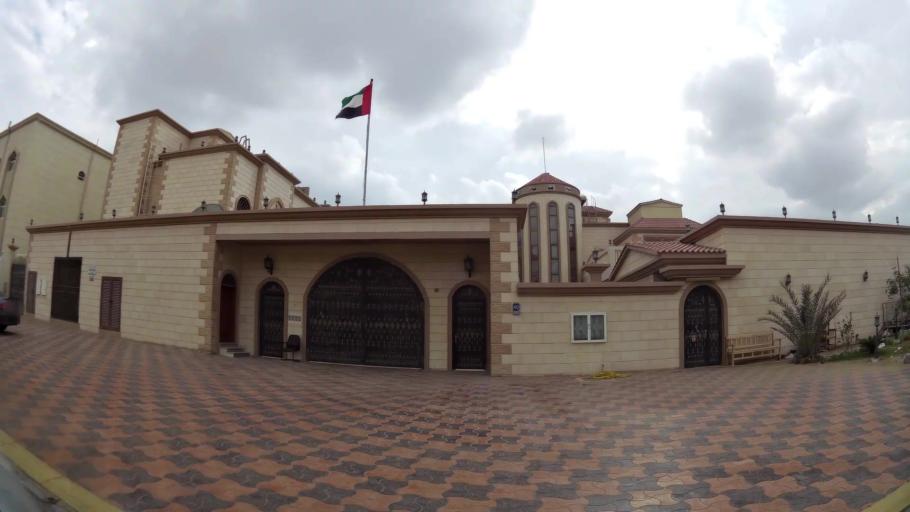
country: AE
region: Abu Dhabi
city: Abu Dhabi
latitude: 24.3555
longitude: 54.6333
